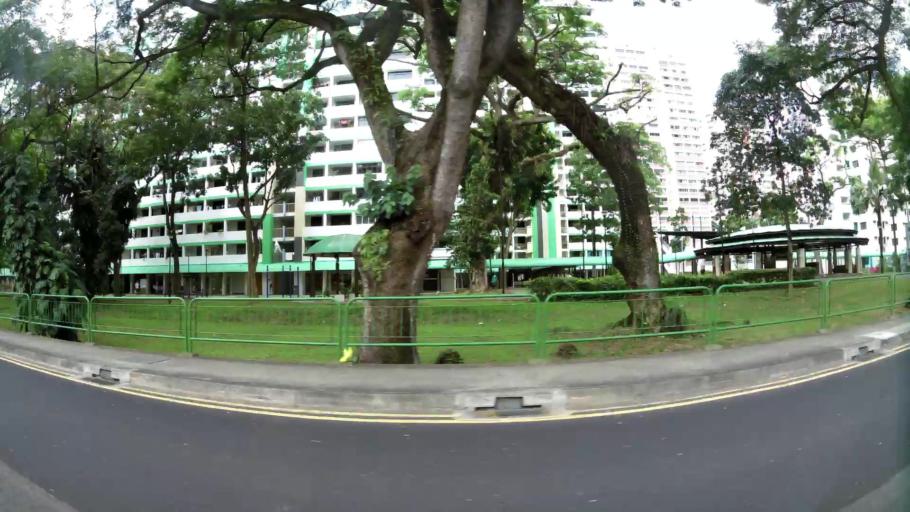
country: SG
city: Singapore
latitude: 1.2907
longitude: 103.8276
